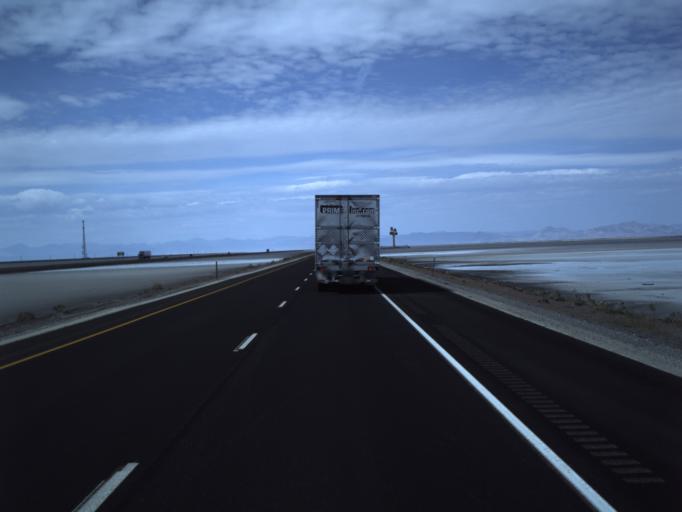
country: US
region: Utah
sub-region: Tooele County
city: Wendover
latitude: 40.7327
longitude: -113.5390
